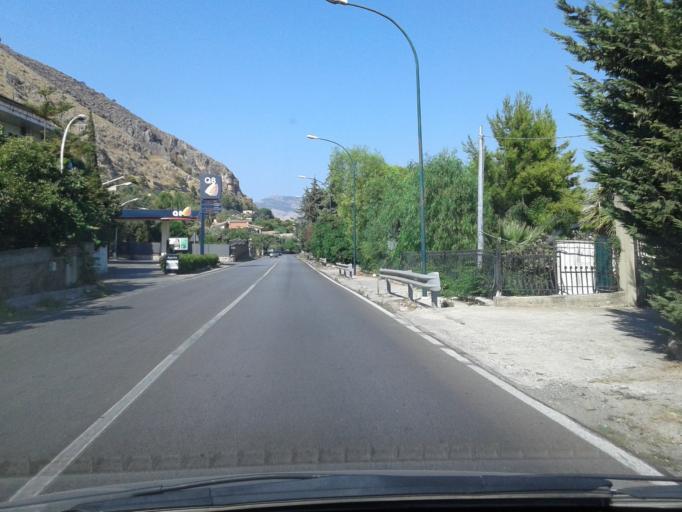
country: IT
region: Sicily
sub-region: Palermo
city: Monreale
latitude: 38.0873
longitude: 13.3020
